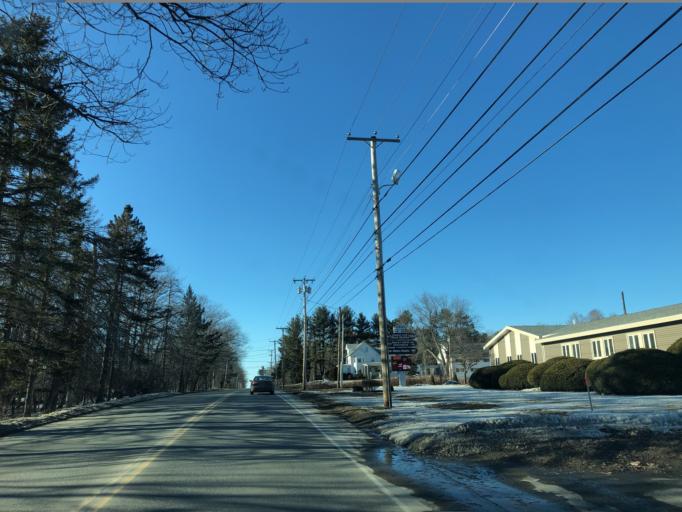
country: US
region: Maine
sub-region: Penobscot County
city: Bangor
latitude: 44.8287
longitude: -68.7843
